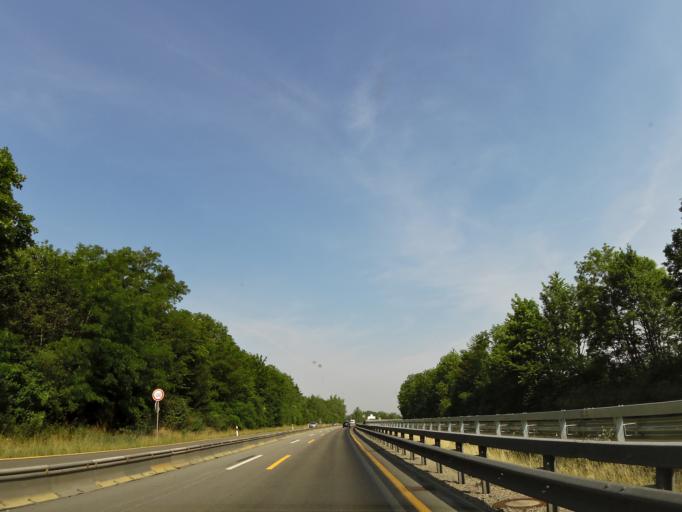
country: DE
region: Rheinland-Pfalz
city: Dintesheim
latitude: 49.7138
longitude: 8.1401
